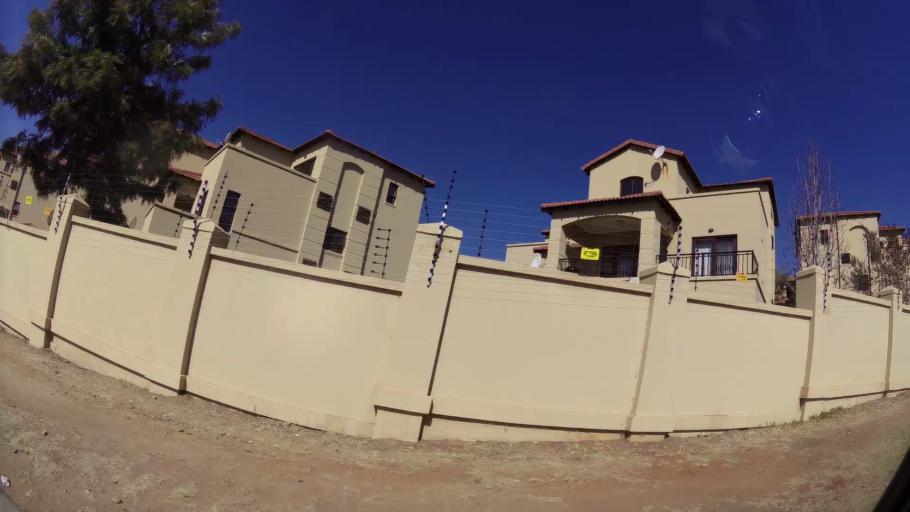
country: ZA
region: Gauteng
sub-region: City of Johannesburg Metropolitan Municipality
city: Midrand
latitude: -25.9704
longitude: 28.1193
